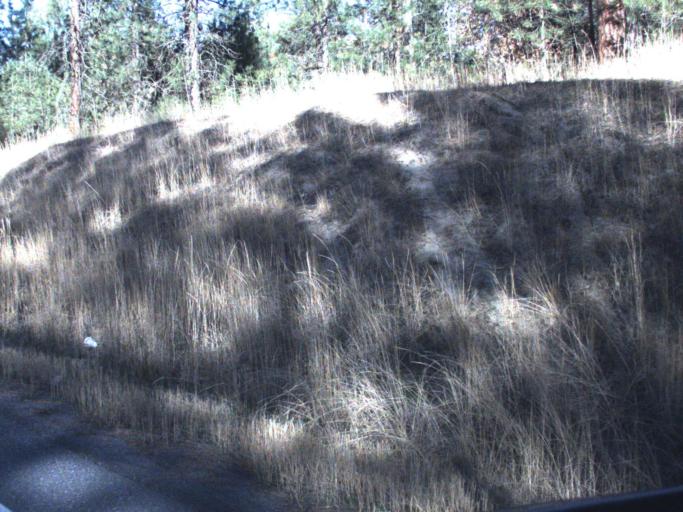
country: US
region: Washington
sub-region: Stevens County
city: Kettle Falls
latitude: 48.6052
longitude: -118.0750
